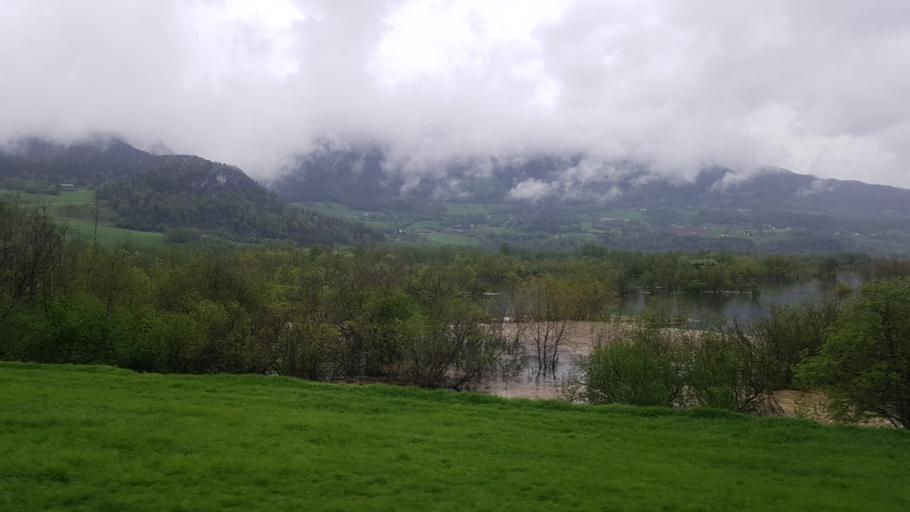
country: NO
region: Oppland
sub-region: Ringebu
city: Ringebu
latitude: 61.4638
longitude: 10.1909
